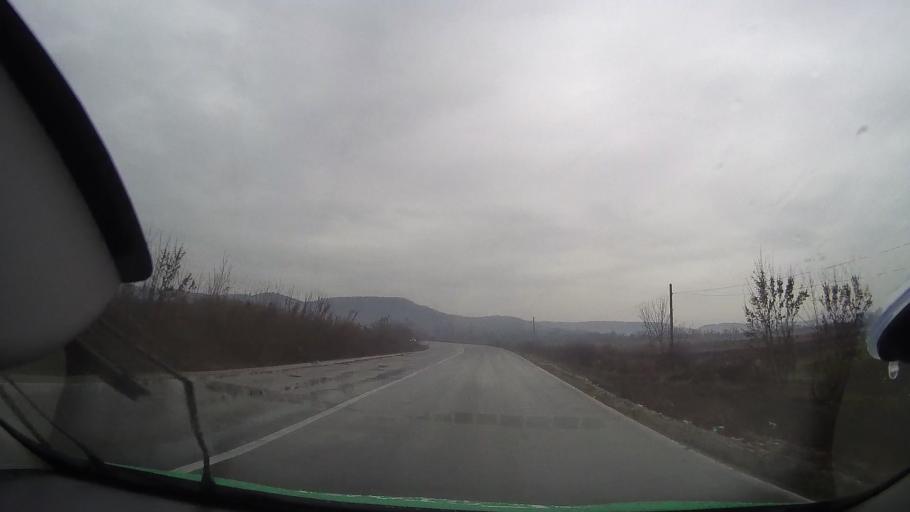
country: RO
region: Bihor
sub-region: Comuna Sambata
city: Sambata
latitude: 46.7950
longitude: 22.2037
